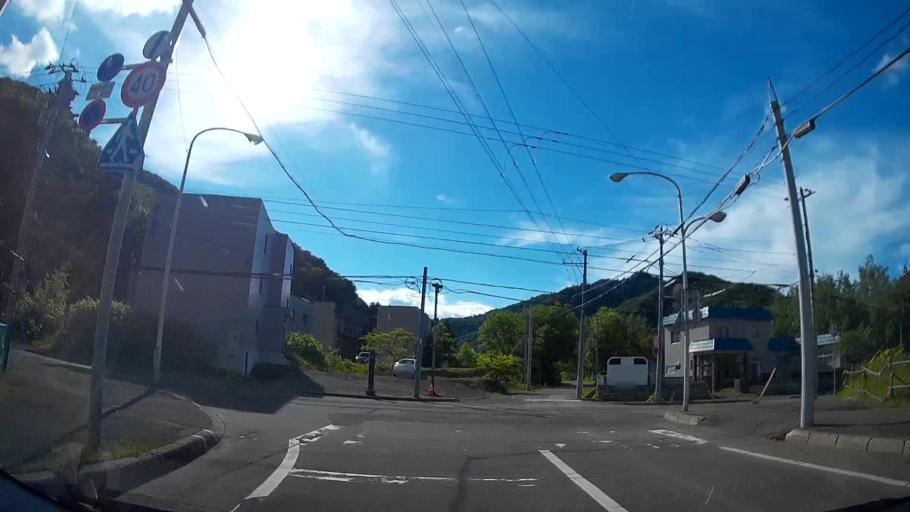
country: JP
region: Hokkaido
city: Sapporo
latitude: 42.9699
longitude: 141.1643
